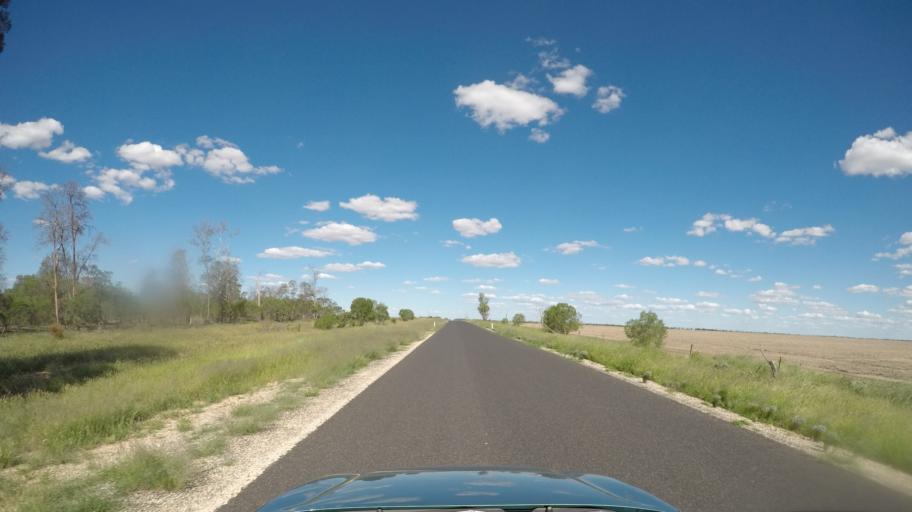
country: AU
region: Queensland
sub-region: Goondiwindi
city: Goondiwindi
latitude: -28.1638
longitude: 150.1600
